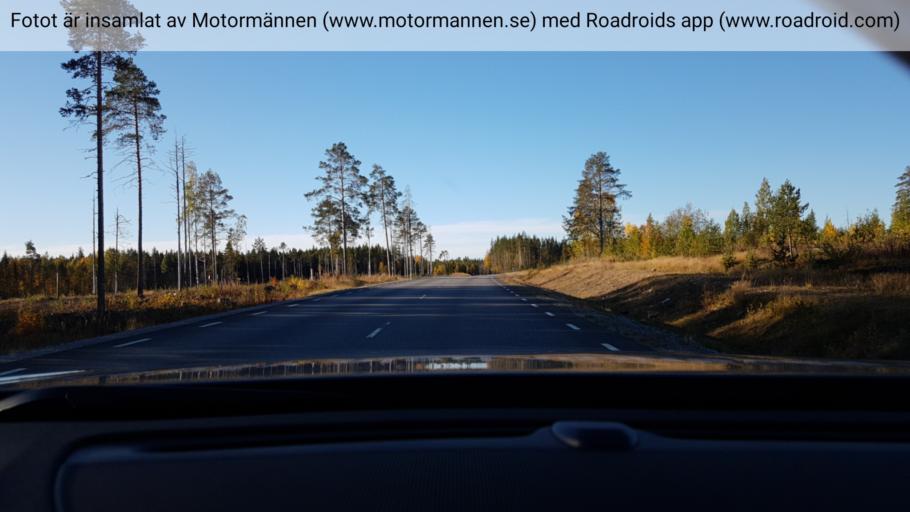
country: SE
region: Norrbotten
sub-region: Pitea Kommun
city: Norrfjarden
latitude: 65.4040
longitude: 21.4613
